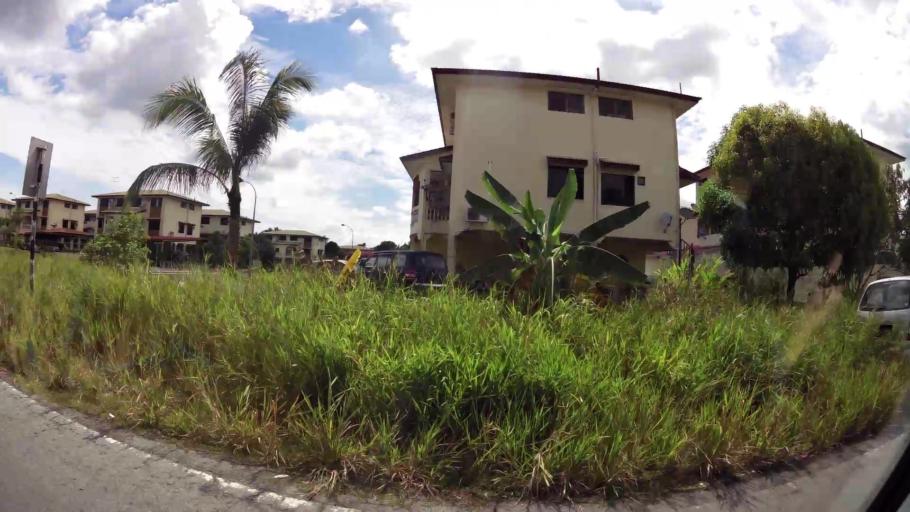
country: BN
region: Brunei and Muara
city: Bandar Seri Begawan
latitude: 4.9311
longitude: 114.8954
